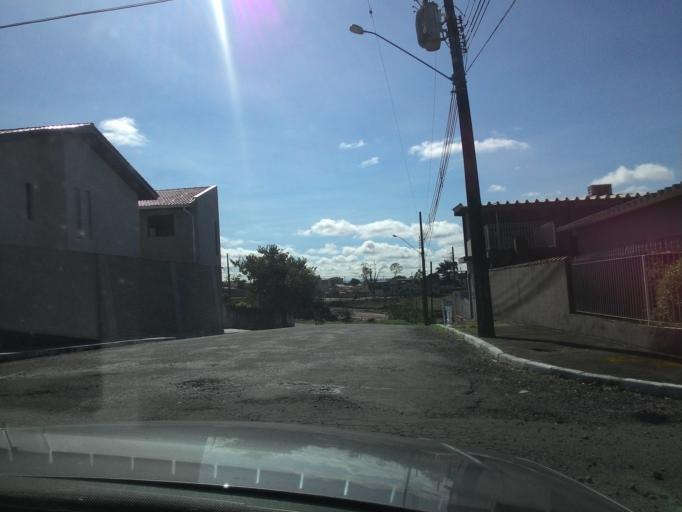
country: BR
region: Sao Paulo
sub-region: Registro
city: Registro
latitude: -24.4990
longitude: -47.8376
